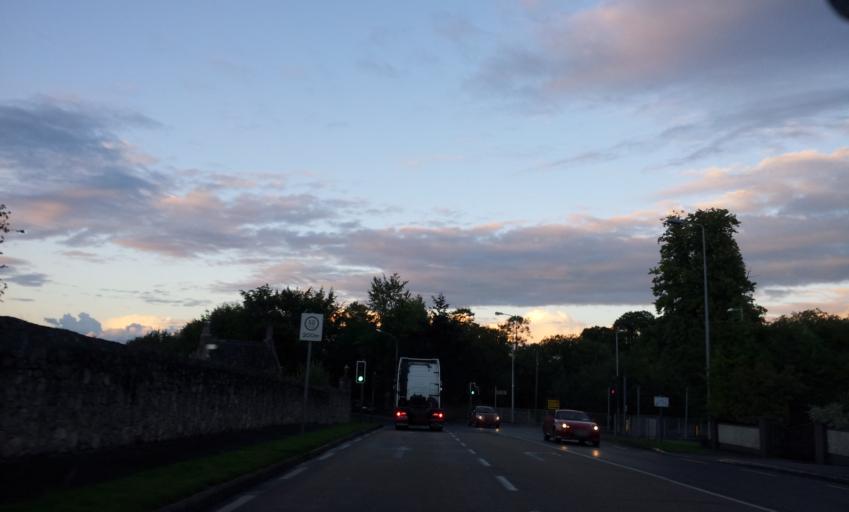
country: IE
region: Munster
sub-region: County Limerick
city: Adare
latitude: 52.5577
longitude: -8.7968
